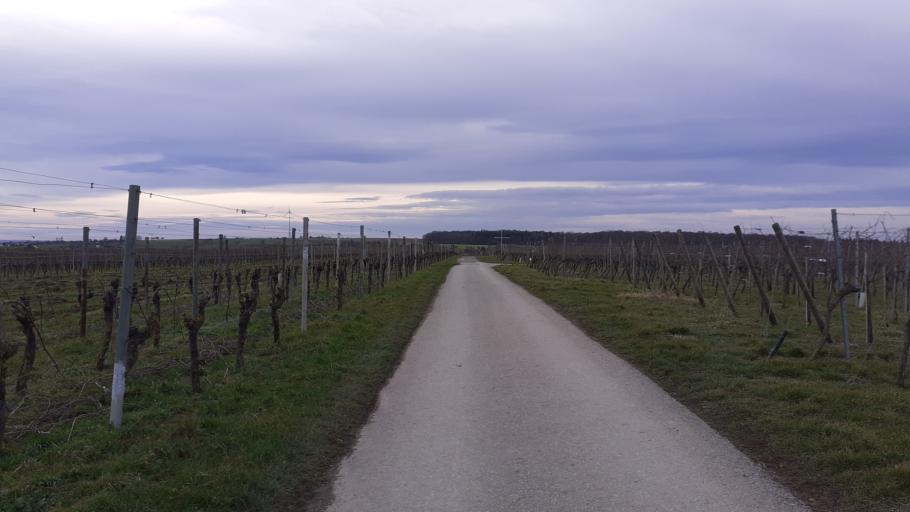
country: DE
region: Baden-Wuerttemberg
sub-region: Regierungsbezirk Stuttgart
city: Mundelsheim
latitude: 48.9865
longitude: 9.2172
